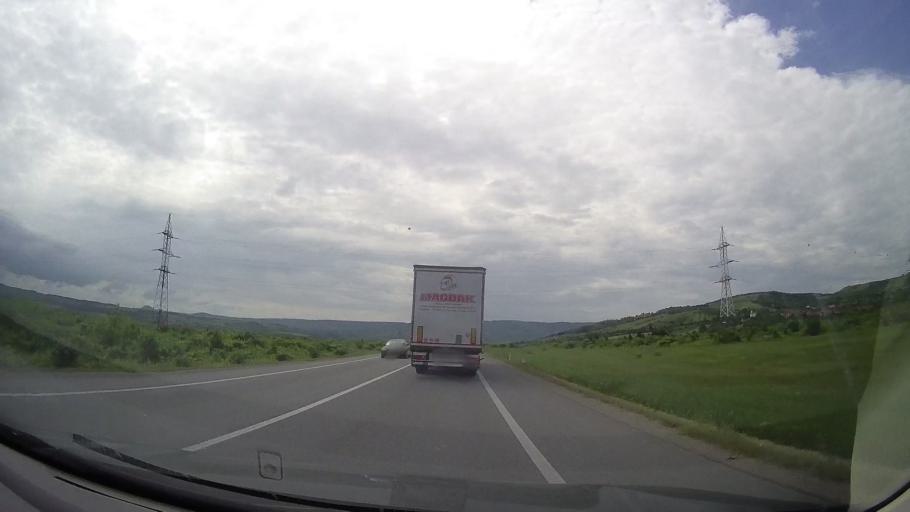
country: RS
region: Central Serbia
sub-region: Borski Okrug
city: Kladovo
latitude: 44.6352
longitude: 22.6037
